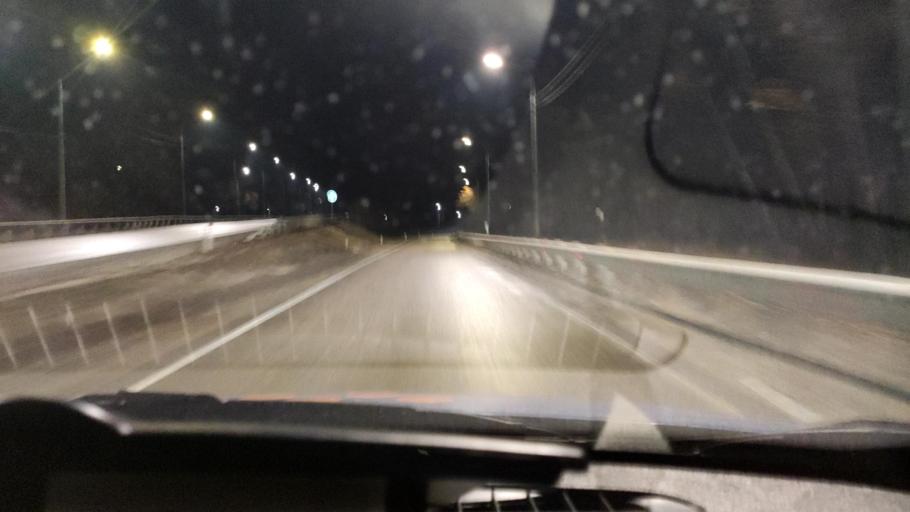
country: RU
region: Voronezj
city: Ramon'
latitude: 51.8890
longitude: 39.2135
